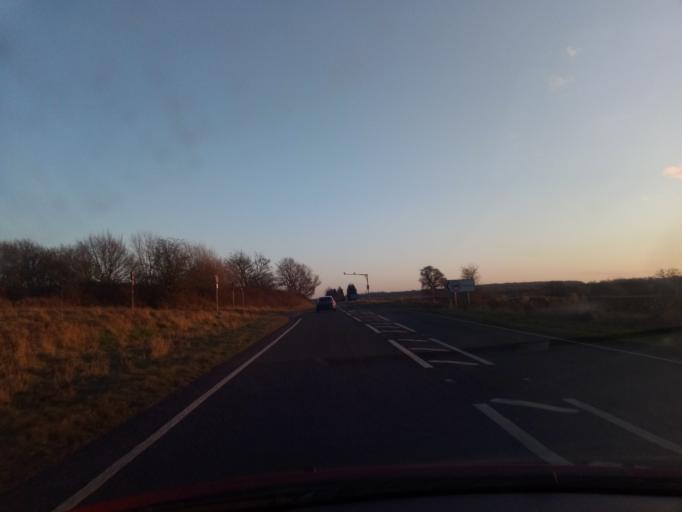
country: GB
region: England
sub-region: Nottinghamshire
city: Burton Joyce
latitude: 53.0435
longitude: -1.0592
